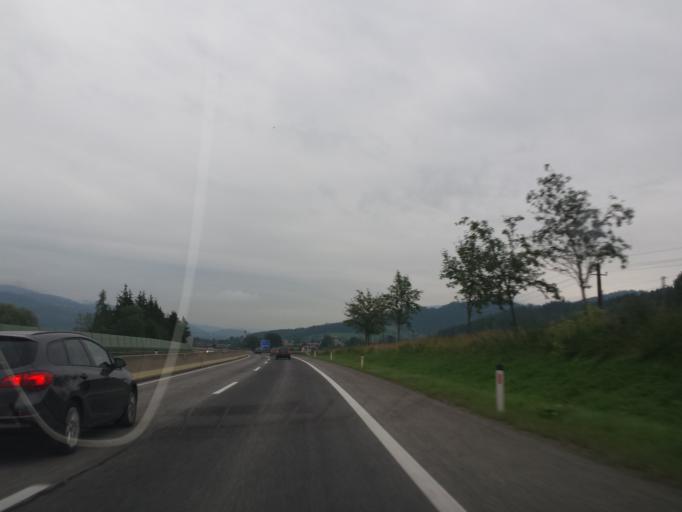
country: AT
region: Styria
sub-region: Politischer Bezirk Bruck-Muerzzuschlag
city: Muerzhofen
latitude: 47.4713
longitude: 15.3870
